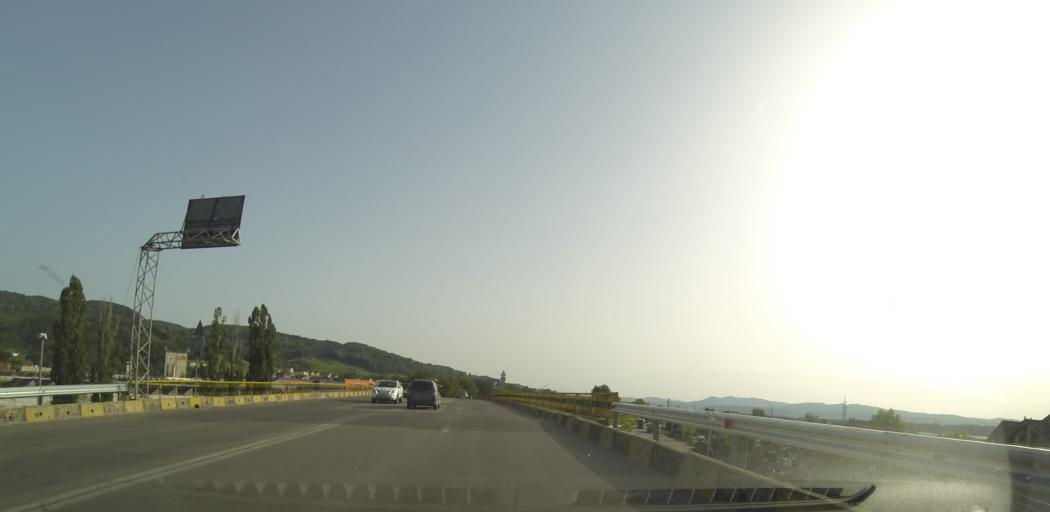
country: RO
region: Valcea
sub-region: Oras Ocnele Mari
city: Ocnele Mari
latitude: 45.0712
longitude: 24.3452
